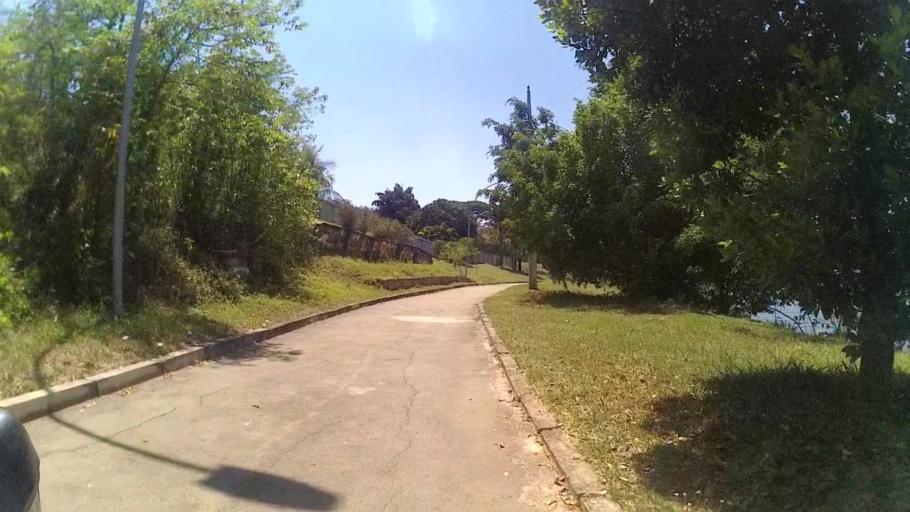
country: BR
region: Federal District
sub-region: Brasilia
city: Brasilia
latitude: -15.7288
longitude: -47.8845
